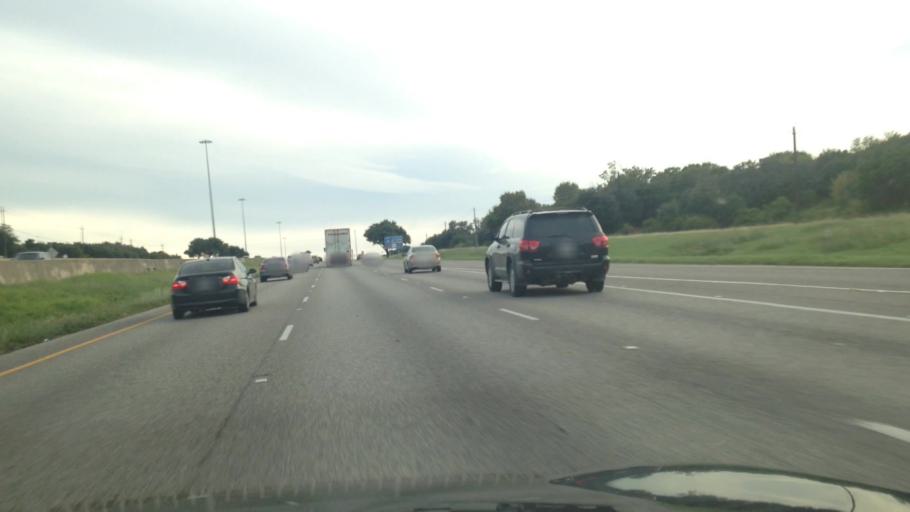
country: US
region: Texas
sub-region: Travis County
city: Onion Creek
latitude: 30.1299
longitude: -97.8002
